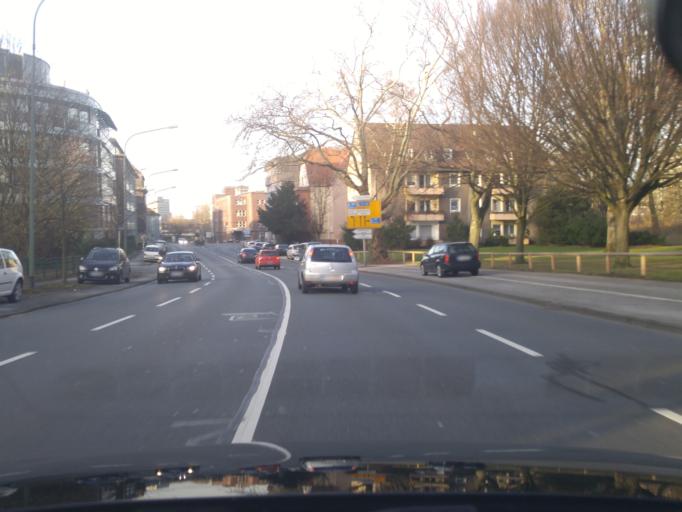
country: DE
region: North Rhine-Westphalia
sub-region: Regierungsbezirk Dusseldorf
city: Essen
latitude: 51.4451
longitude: 7.0221
